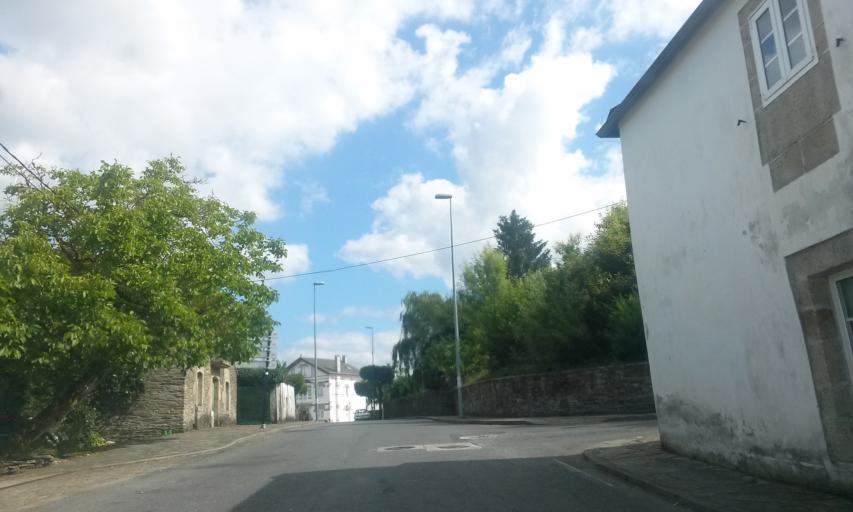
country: ES
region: Galicia
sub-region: Provincia de Lugo
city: Outeiro de Rei
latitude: 43.1026
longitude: -7.6142
